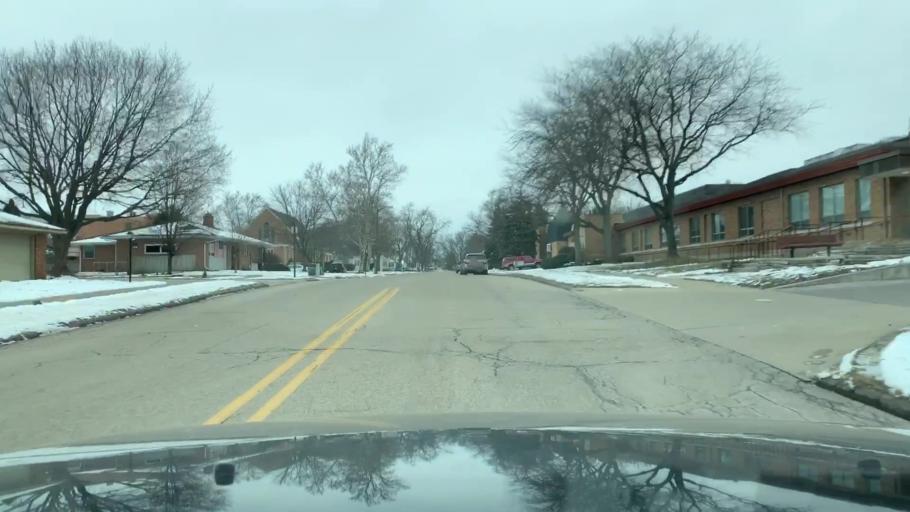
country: US
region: Michigan
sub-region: Ottawa County
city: Zeeland
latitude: 42.8088
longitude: -86.0246
